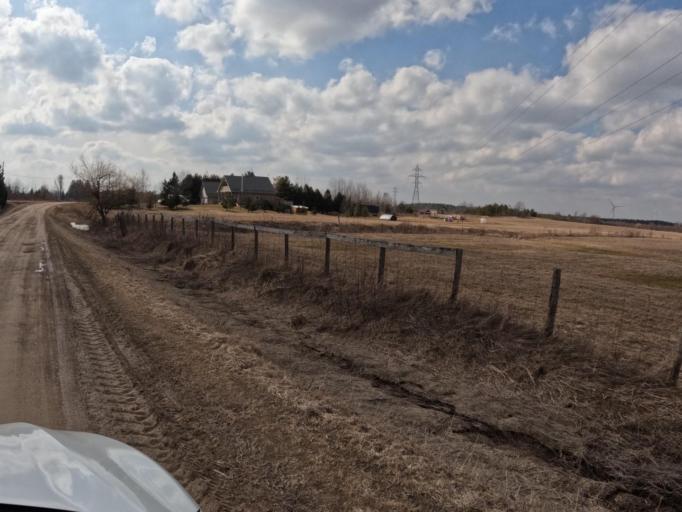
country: CA
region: Ontario
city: Shelburne
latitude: 43.9614
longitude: -80.3058
